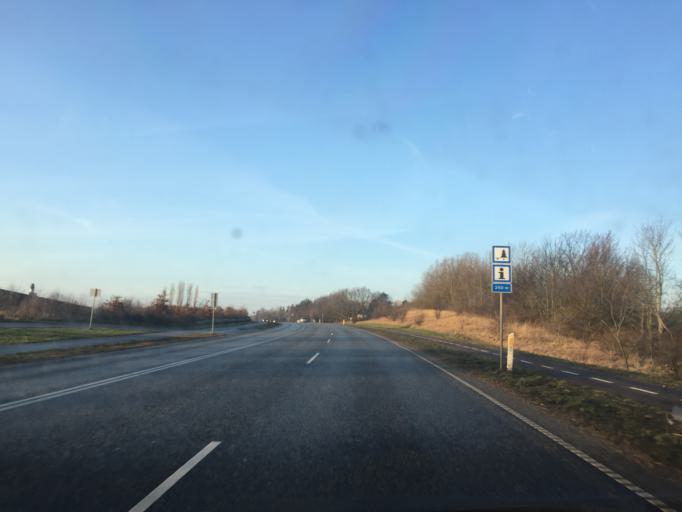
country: DK
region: Zealand
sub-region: Slagelse Kommune
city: Slagelse
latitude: 55.3844
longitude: 11.3702
